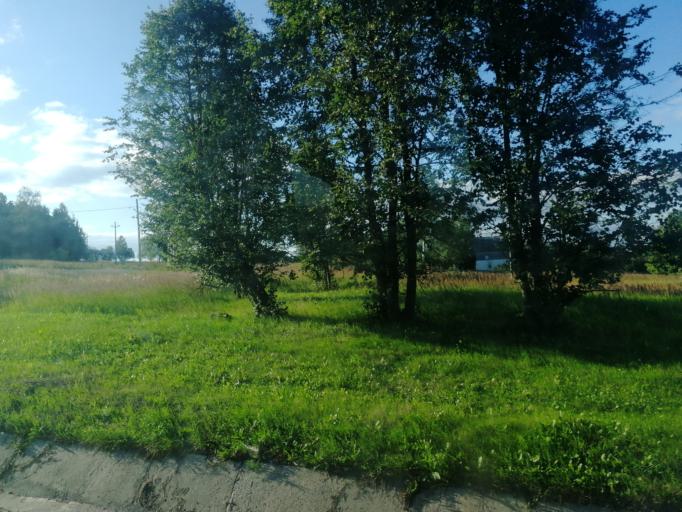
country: RU
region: Tula
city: Dubna
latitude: 54.2813
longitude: 37.1734
